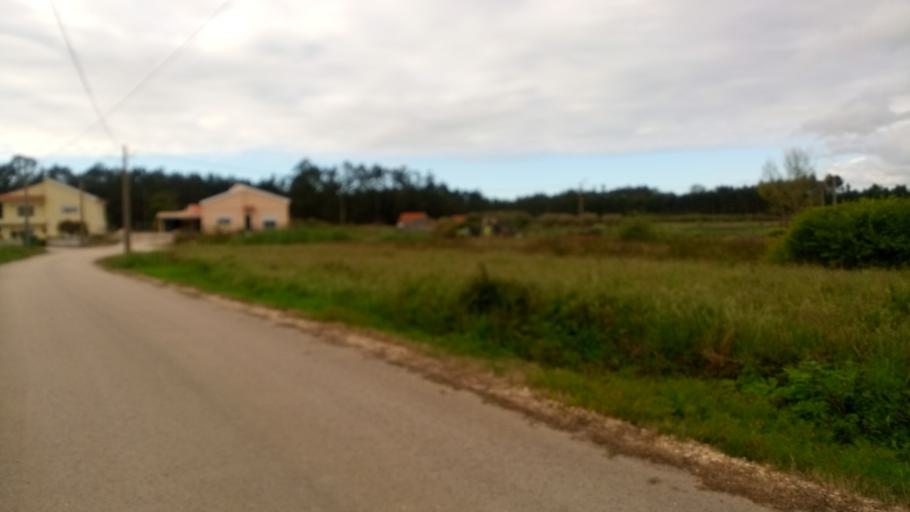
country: PT
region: Leiria
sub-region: Caldas da Rainha
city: Caldas da Rainha
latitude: 39.4550
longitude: -9.1743
